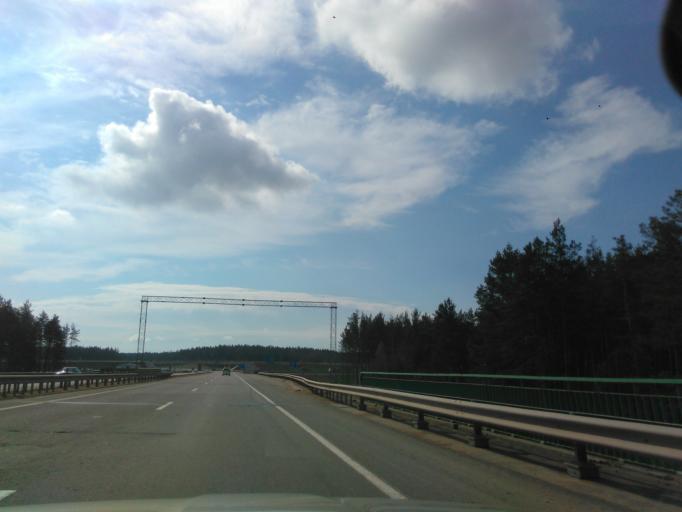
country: BY
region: Minsk
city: Rakaw
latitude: 53.9690
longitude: 27.0831
